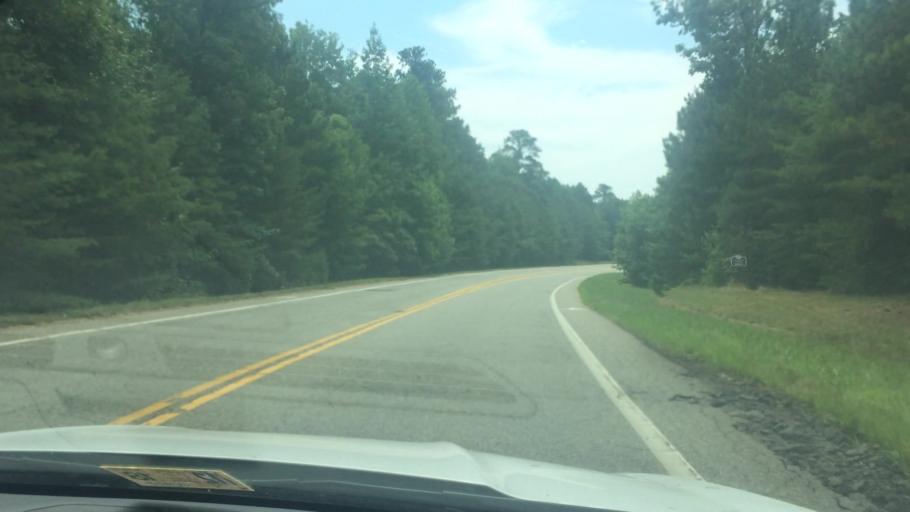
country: US
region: Virginia
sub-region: James City County
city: Williamsburg
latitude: 37.2678
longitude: -76.8063
